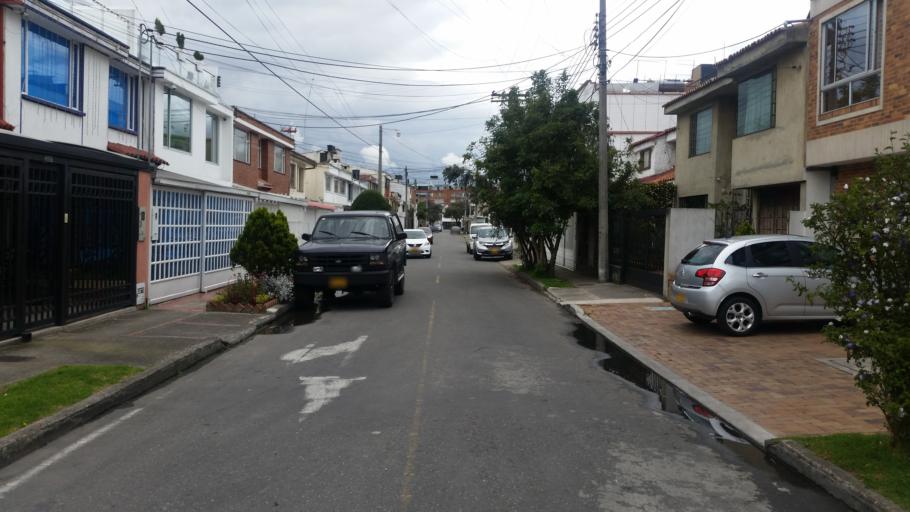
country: CO
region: Bogota D.C.
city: Bogota
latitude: 4.6708
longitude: -74.1107
